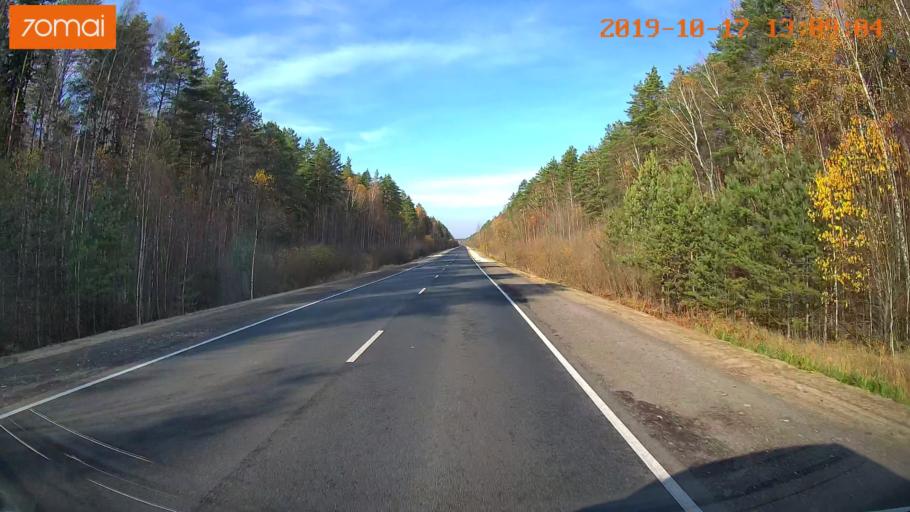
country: RU
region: Rjazan
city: Syntul
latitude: 54.9981
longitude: 41.2654
